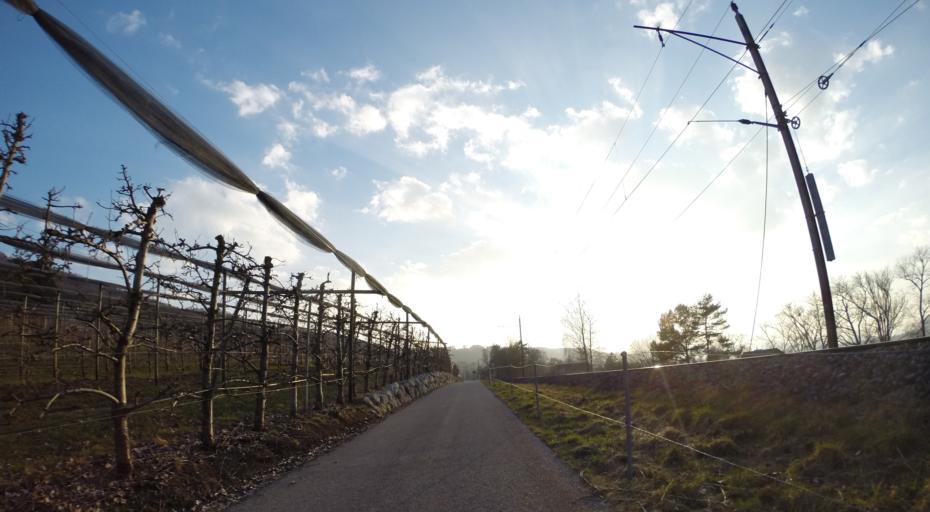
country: DE
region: Baden-Wuerttemberg
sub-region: Freiburg Region
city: Ohningen
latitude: 47.6491
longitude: 8.9294
